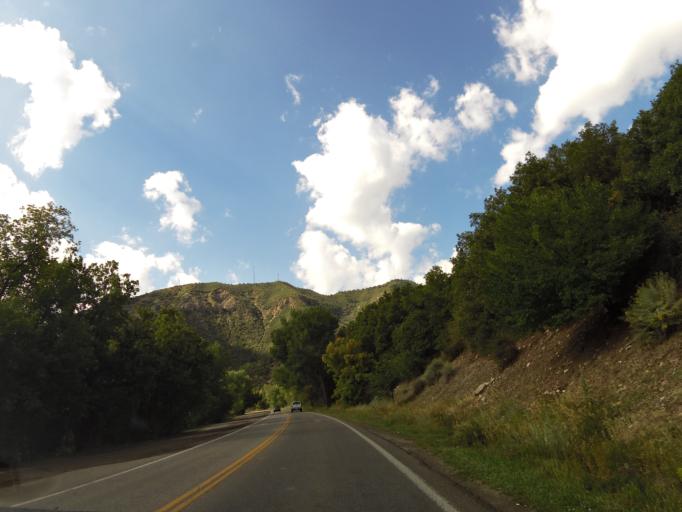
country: US
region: Colorado
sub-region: La Plata County
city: Durango
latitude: 37.2741
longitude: -107.8856
